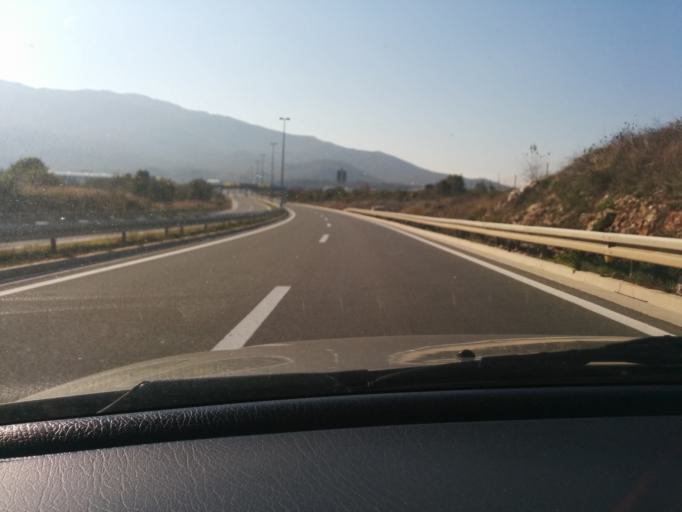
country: HR
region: Splitsko-Dalmatinska
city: Dugopolje
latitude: 43.6009
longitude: 16.5779
